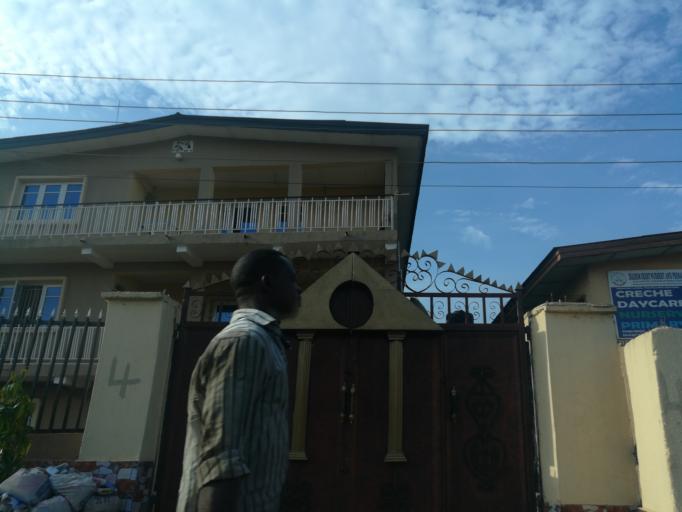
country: NG
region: Lagos
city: Ikeja
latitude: 6.5939
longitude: 3.3464
